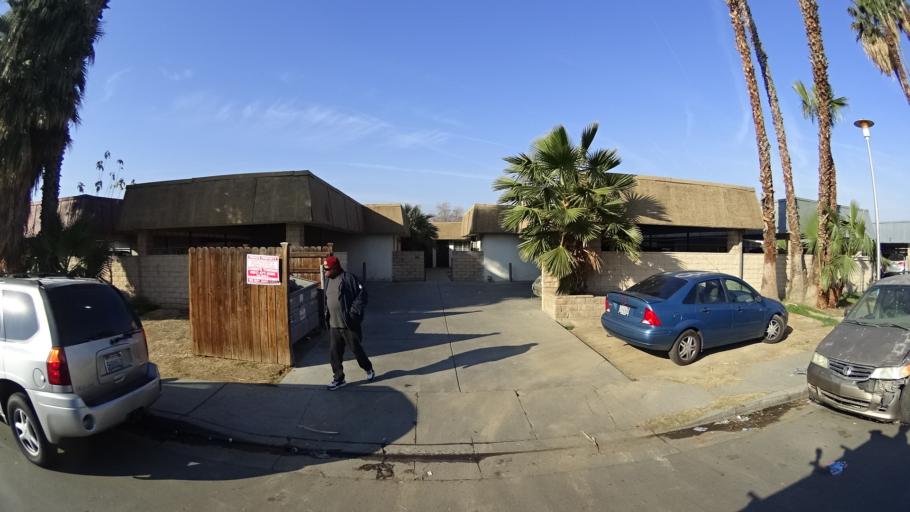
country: US
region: California
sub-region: Kern County
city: Greenfield
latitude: 35.3153
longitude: -119.0203
